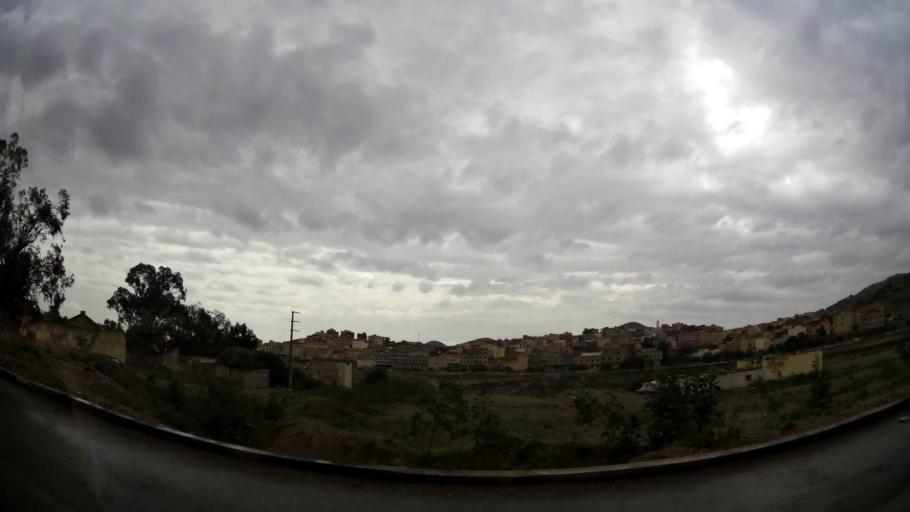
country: MA
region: Oriental
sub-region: Nador
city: Nador
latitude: 35.1487
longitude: -3.0081
